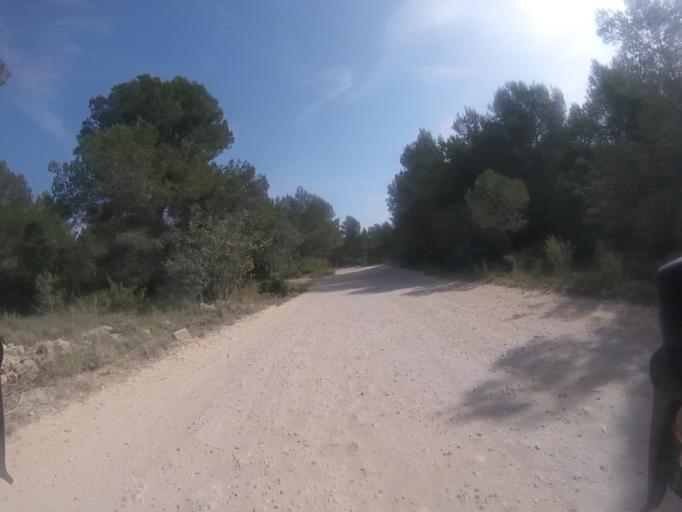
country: ES
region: Valencia
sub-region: Provincia de Castello
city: Alcoceber
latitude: 40.2677
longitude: 0.3010
